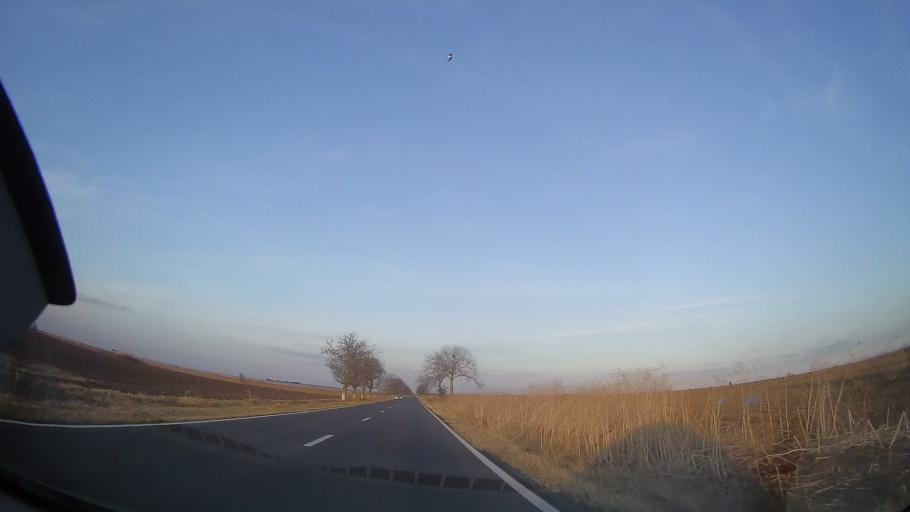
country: RO
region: Constanta
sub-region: Comuna Topraisar
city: Topraisar
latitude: 43.9928
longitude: 28.4268
